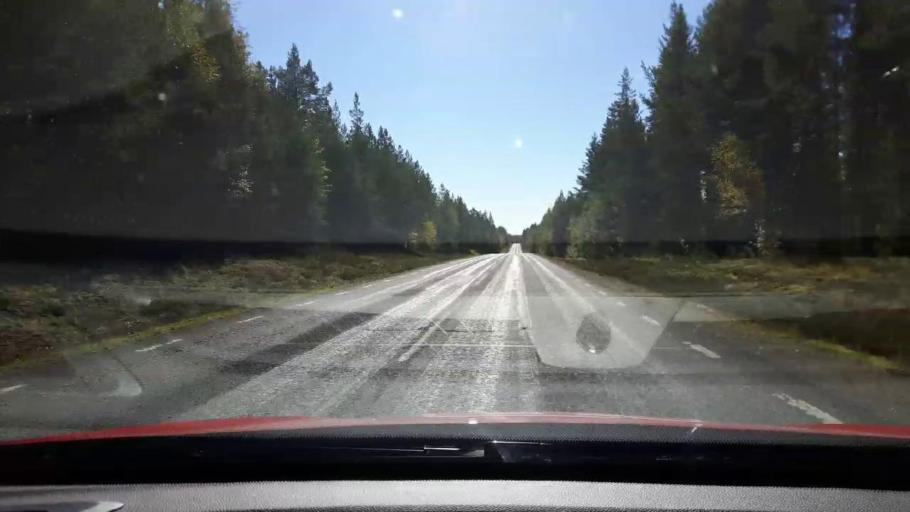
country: SE
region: Jaemtland
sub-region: Harjedalens Kommun
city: Sveg
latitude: 62.3493
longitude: 14.0314
